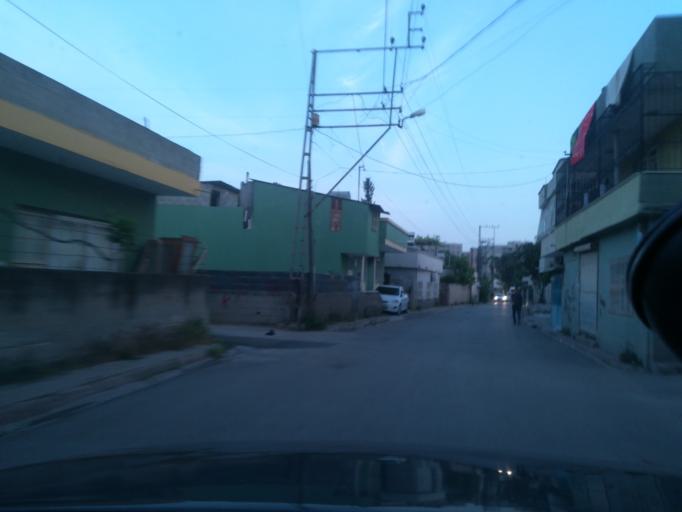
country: TR
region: Adana
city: Seyhan
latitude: 37.0143
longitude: 35.2800
